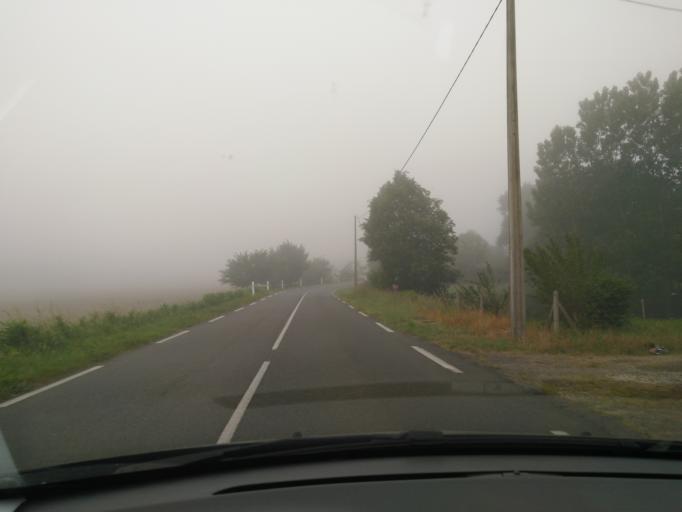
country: FR
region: Aquitaine
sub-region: Departement des Landes
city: Villeneuve-de-Marsan
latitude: 43.8874
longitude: -0.3263
